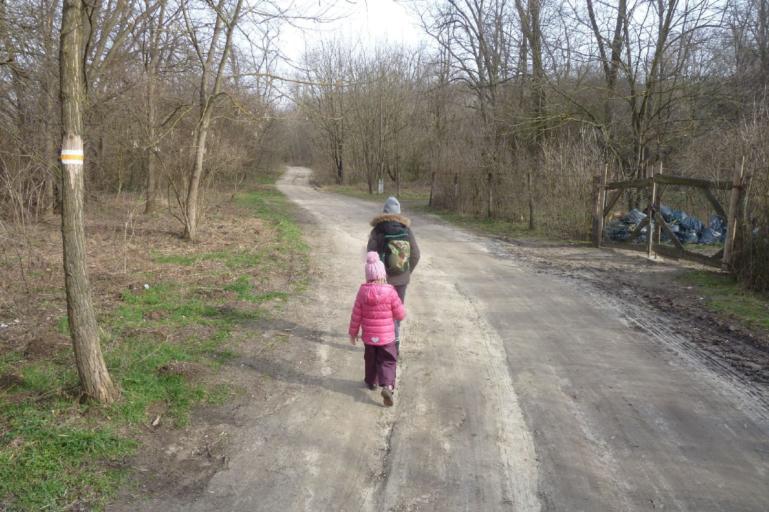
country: HU
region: Pest
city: Pecel
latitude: 47.5013
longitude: 19.3371
